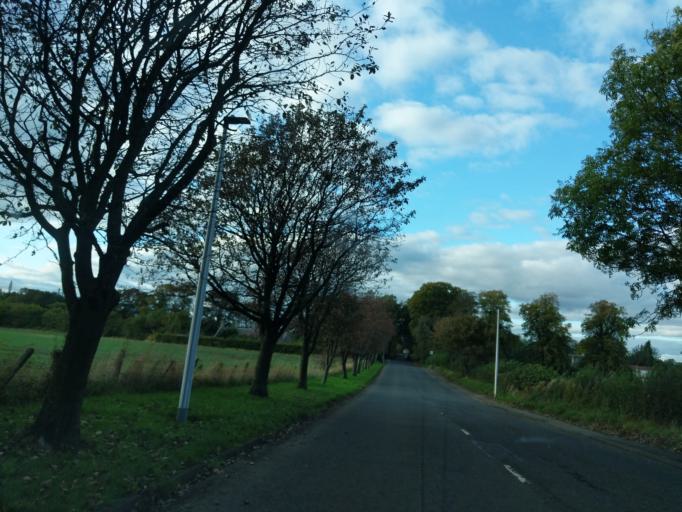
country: GB
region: Scotland
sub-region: Edinburgh
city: Queensferry
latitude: 55.9855
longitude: -3.3756
